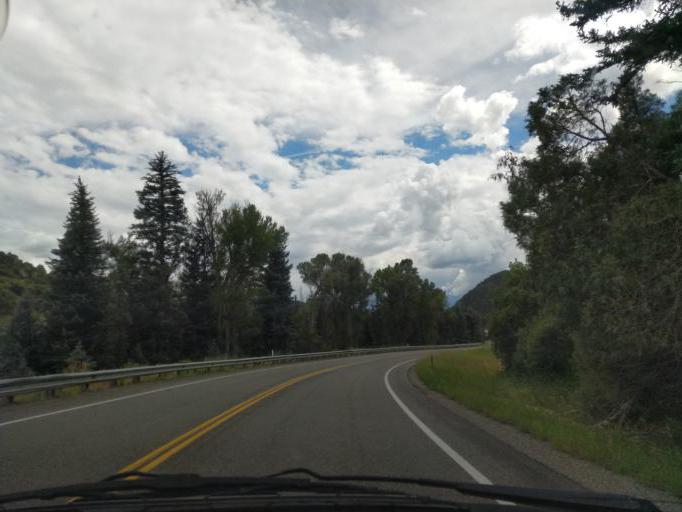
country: US
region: Colorado
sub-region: Delta County
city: Paonia
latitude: 39.0585
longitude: -107.3632
